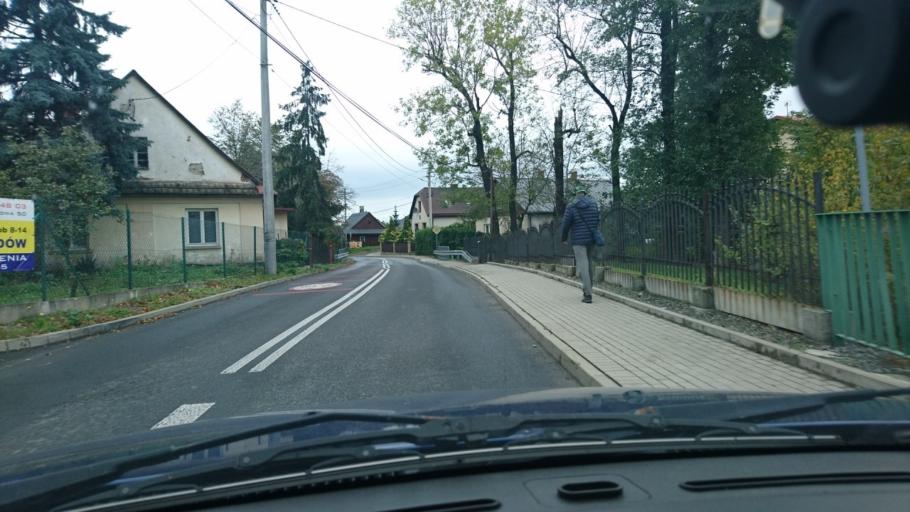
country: PL
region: Silesian Voivodeship
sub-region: Powiat bielski
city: Kozy
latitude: 49.8484
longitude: 19.1382
